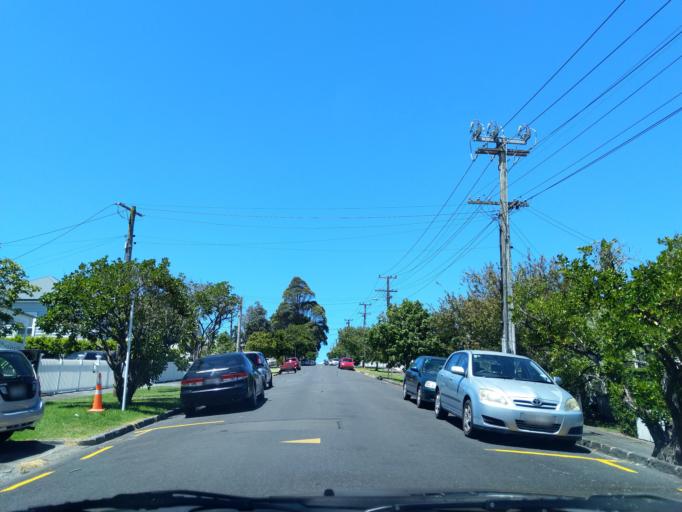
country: NZ
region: Auckland
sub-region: Auckland
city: Auckland
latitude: -36.8699
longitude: 174.7413
